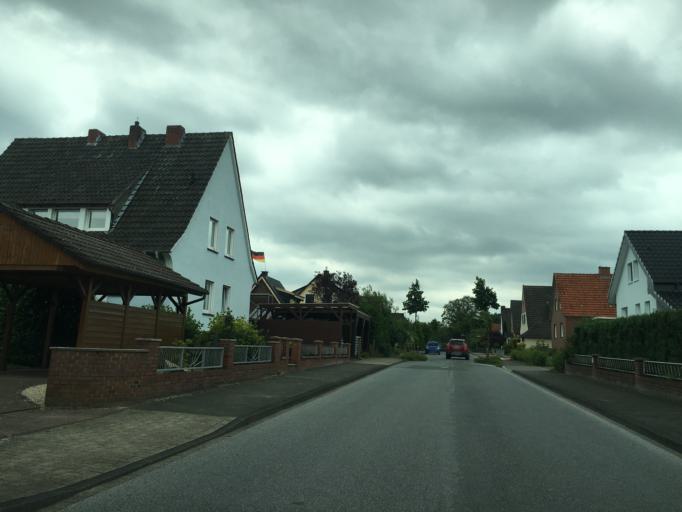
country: DE
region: North Rhine-Westphalia
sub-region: Regierungsbezirk Munster
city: Steinfurt
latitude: 52.1486
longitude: 7.3201
